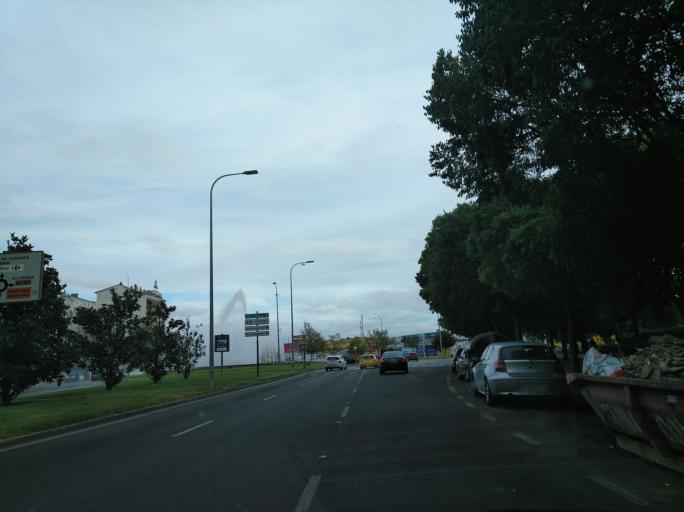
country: ES
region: Extremadura
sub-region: Provincia de Badajoz
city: Badajoz
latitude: 38.8657
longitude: -6.9840
